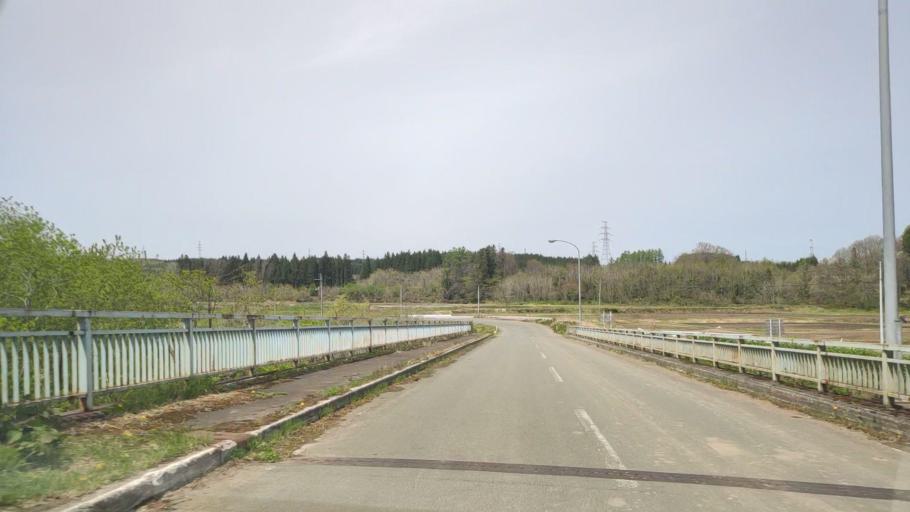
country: JP
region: Aomori
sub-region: Misawa Shi
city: Inuotose
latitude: 40.7811
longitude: 141.1208
